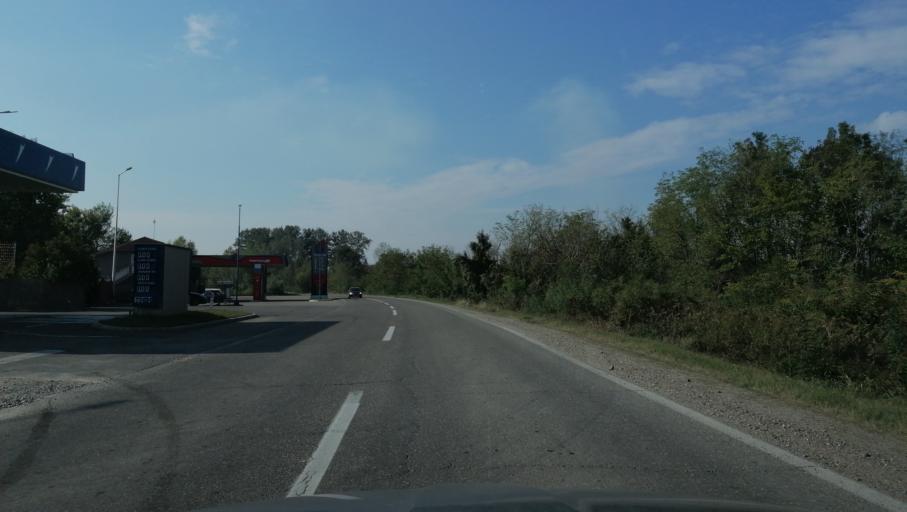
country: BA
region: Republika Srpska
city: Popovi
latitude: 44.7797
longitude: 19.3175
